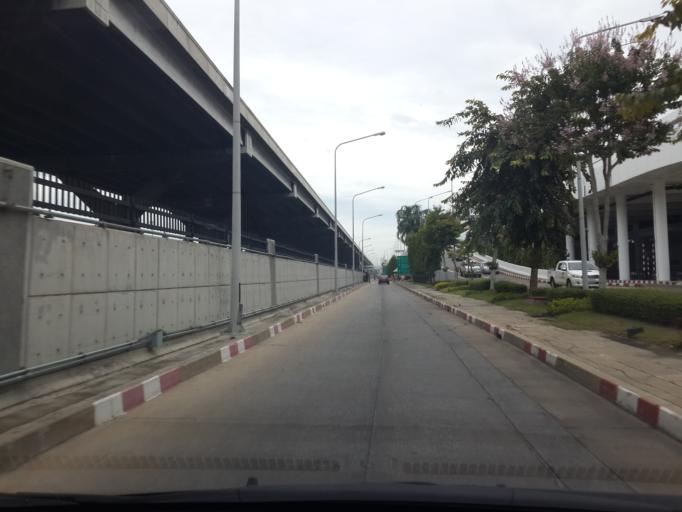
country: TH
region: Bangkok
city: Don Mueang
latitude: 13.9161
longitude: 100.5996
